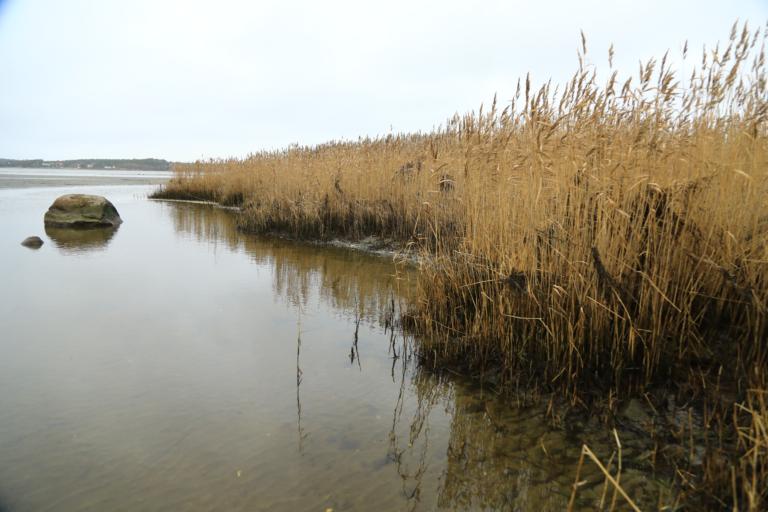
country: SE
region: Halland
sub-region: Varbergs Kommun
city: Varberg
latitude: 57.1812
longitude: 12.2134
